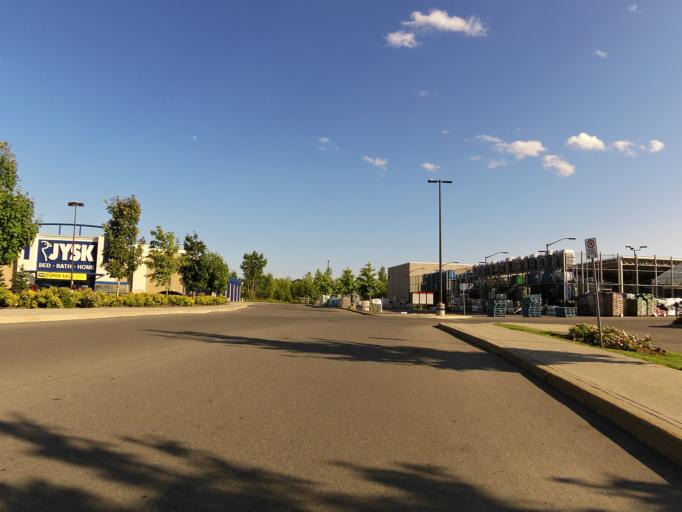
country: CA
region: Ontario
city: Ottawa
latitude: 45.3384
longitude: -75.7132
